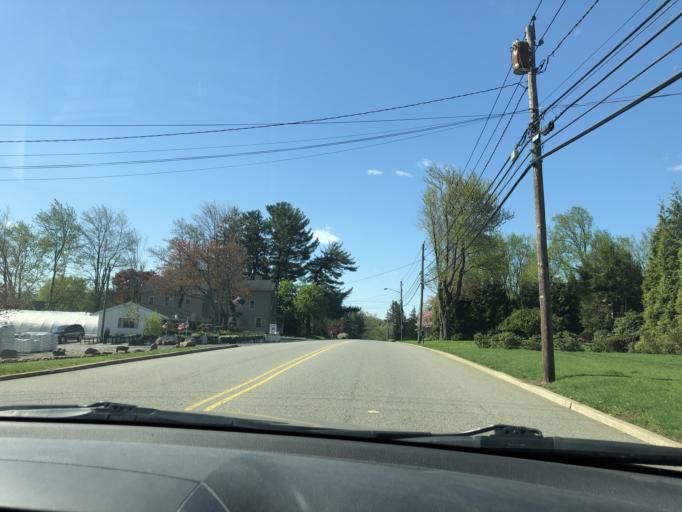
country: US
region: New Jersey
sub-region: Essex County
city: North Caldwell
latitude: 40.8507
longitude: -74.2594
